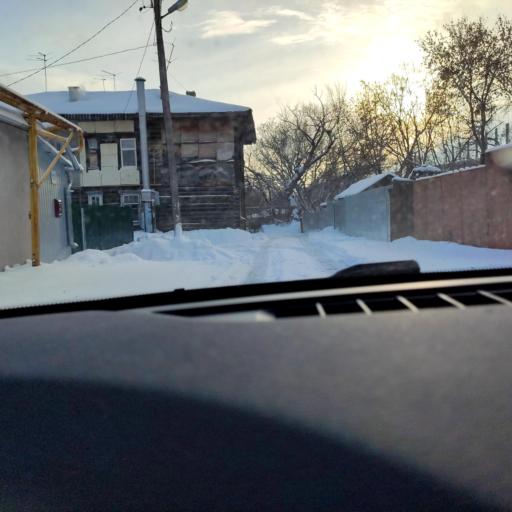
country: RU
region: Samara
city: Samara
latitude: 53.1824
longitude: 50.1150
